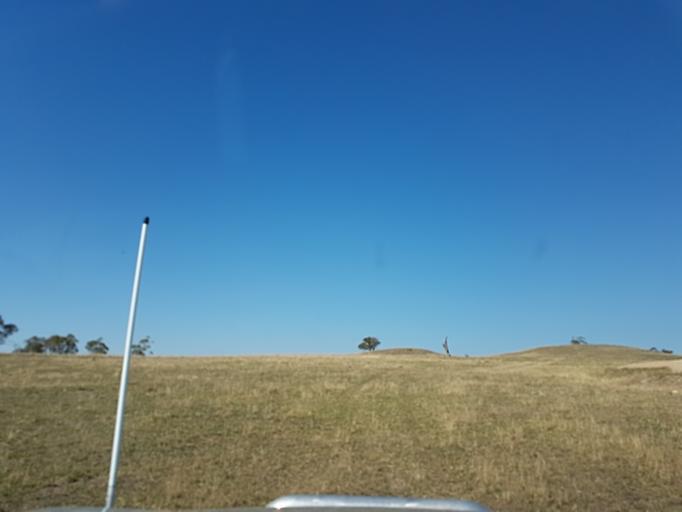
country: AU
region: New South Wales
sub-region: Snowy River
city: Jindabyne
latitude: -37.0459
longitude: 148.2963
